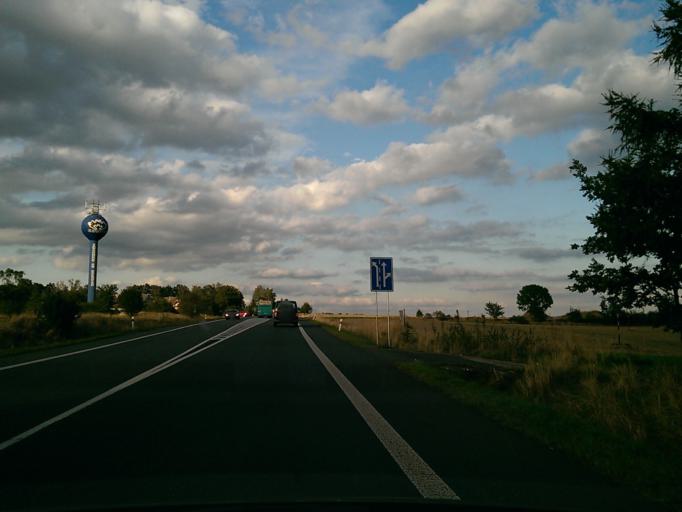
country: CZ
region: Central Bohemia
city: Dolni Bousov
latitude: 50.4537
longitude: 15.0874
